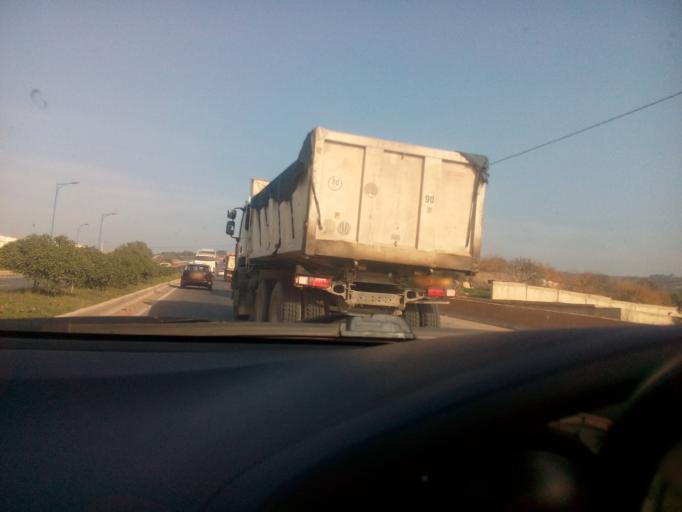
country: DZ
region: Oran
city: Es Senia
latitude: 35.6290
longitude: -0.7169
